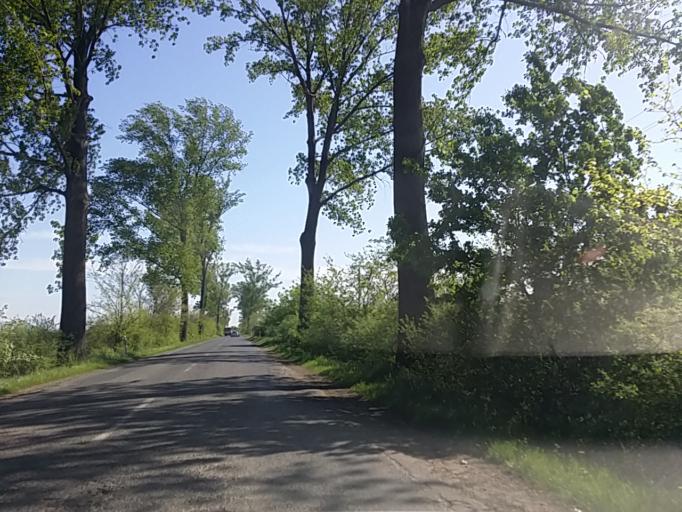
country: HU
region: Bekes
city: Bekes
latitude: 46.7114
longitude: 21.1806
